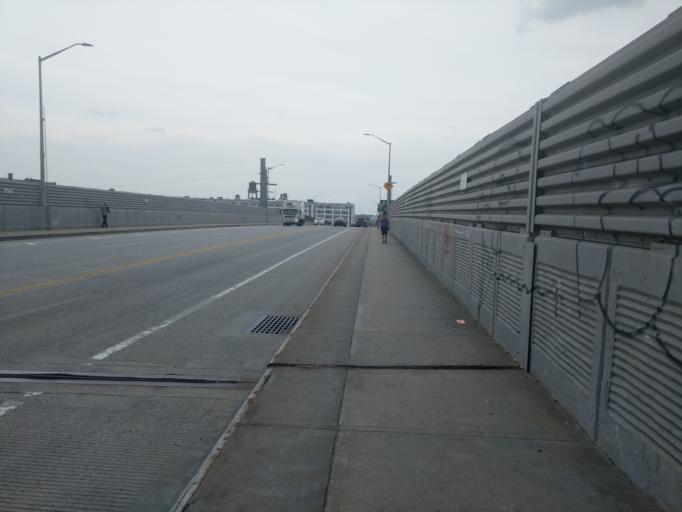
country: US
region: New York
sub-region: Queens County
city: Long Island City
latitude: 40.7481
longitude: -73.9253
